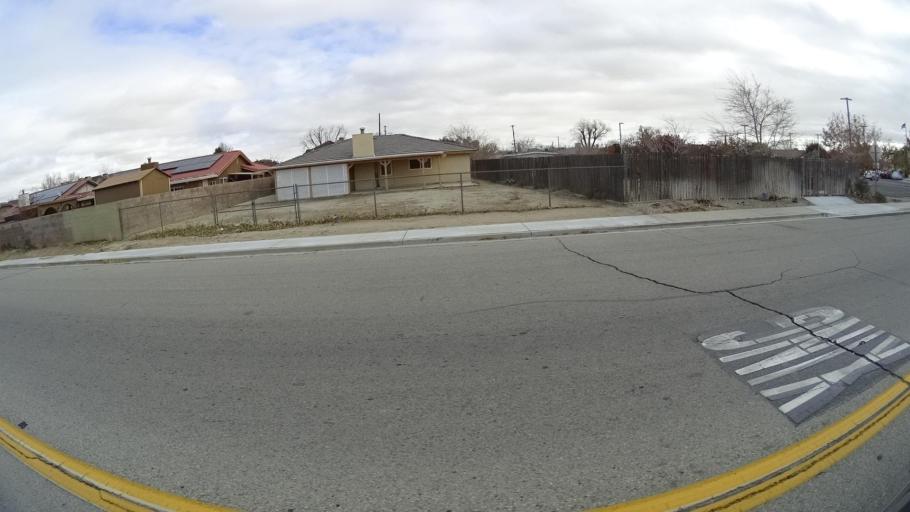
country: US
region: California
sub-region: Kern County
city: Rosamond
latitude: 34.8584
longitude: -118.1671
